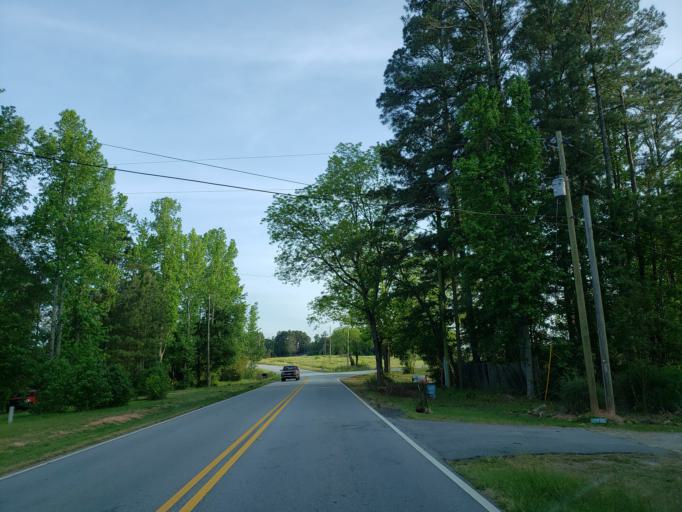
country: US
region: Georgia
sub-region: Carroll County
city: Mount Zion
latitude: 33.6227
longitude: -85.1793
